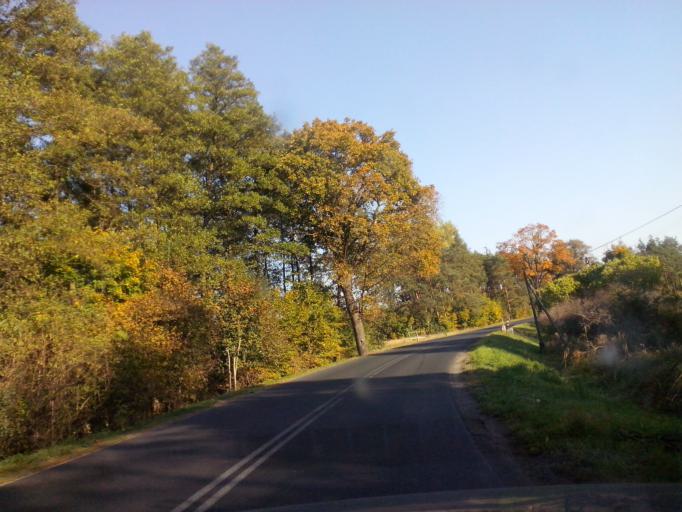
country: PL
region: Kujawsko-Pomorskie
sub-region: Powiat brodnicki
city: Bartniczka
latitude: 53.2474
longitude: 19.6365
